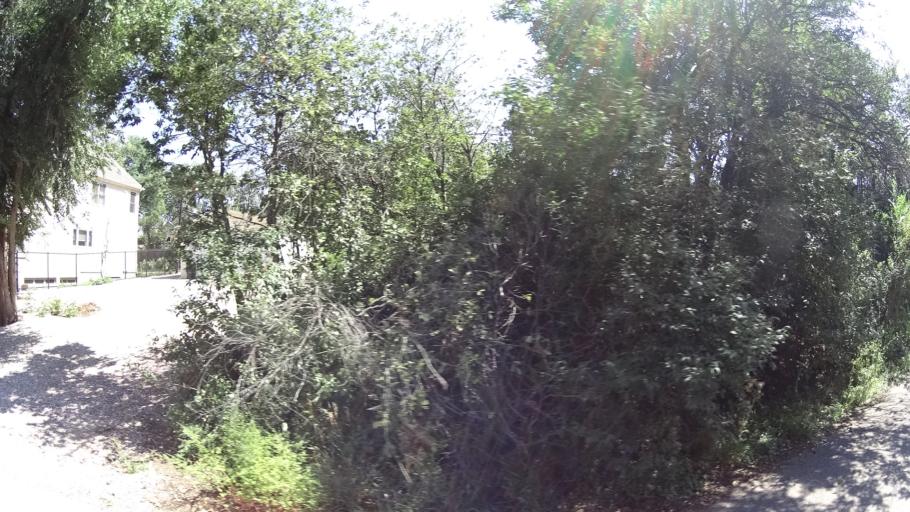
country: US
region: Colorado
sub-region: El Paso County
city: Colorado Springs
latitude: 38.8646
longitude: -104.8266
